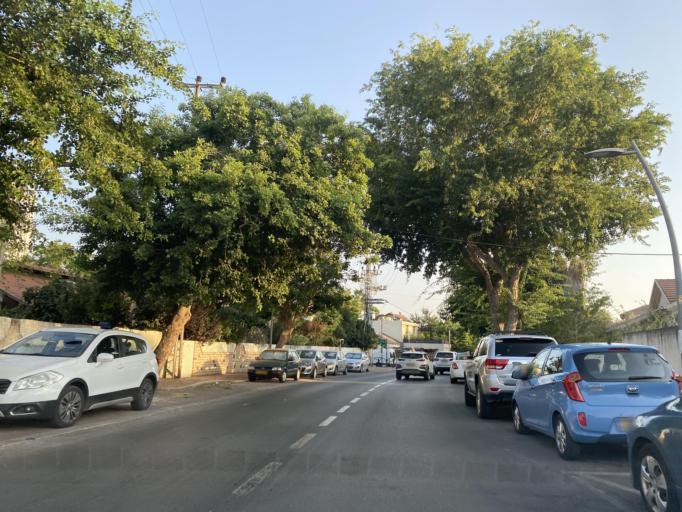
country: IL
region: Tel Aviv
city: Ramat HaSharon
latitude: 32.1350
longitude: 34.8567
